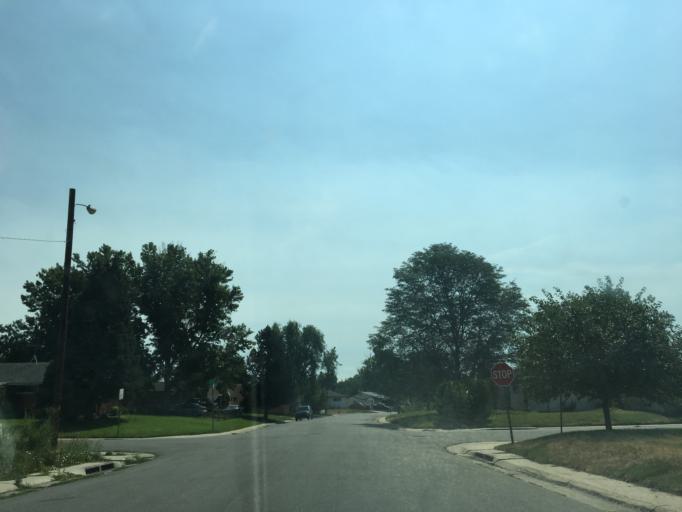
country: US
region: Colorado
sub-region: Jefferson County
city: Lakewood
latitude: 39.6924
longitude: -105.0488
